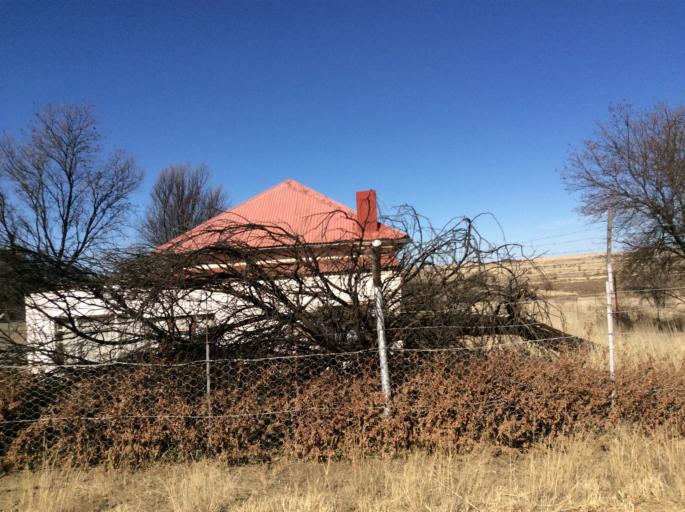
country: ZA
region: Orange Free State
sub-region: Lejweleputswa District Municipality
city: Brandfort
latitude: -28.7220
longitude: 26.0652
